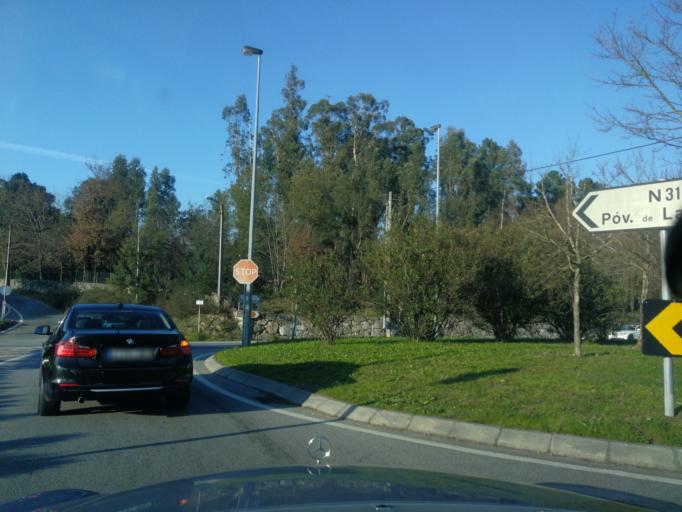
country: PT
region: Braga
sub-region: Guimaraes
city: Ponte
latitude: 41.4919
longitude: -8.3390
